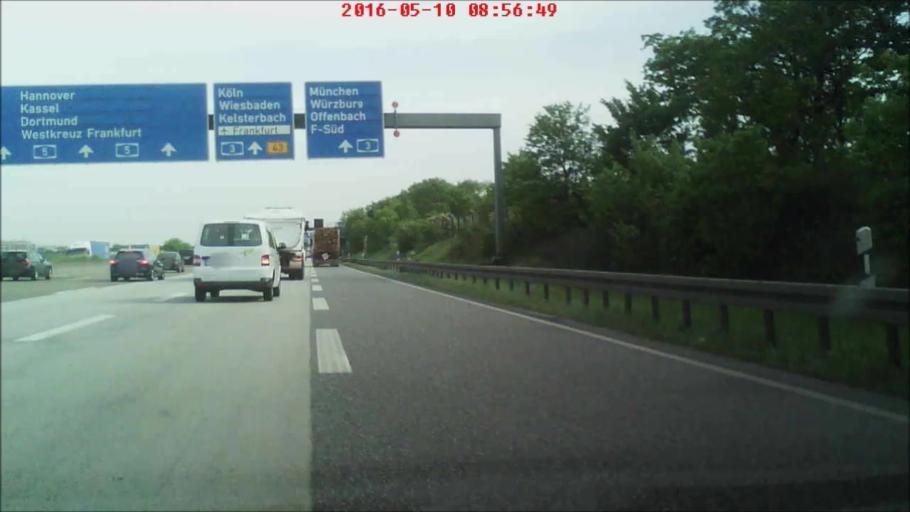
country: DE
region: Hesse
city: Morfelden-Walldorf
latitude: 50.0401
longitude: 8.5981
